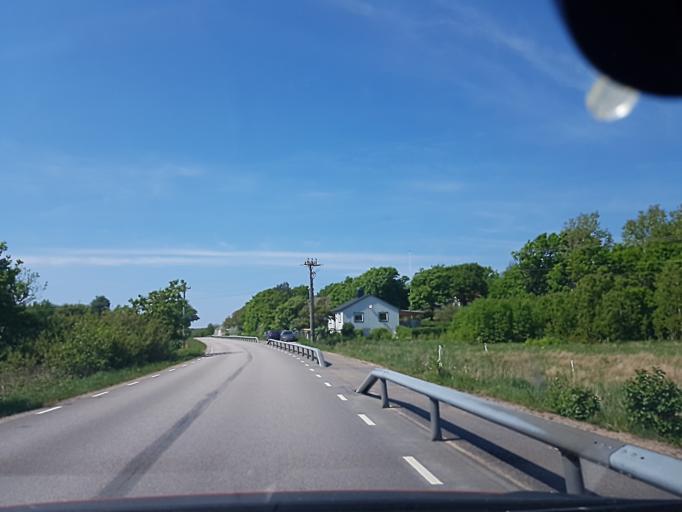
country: SE
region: Vaestra Goetaland
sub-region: Lysekils Kommun
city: Lysekil
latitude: 58.1642
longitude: 11.4420
